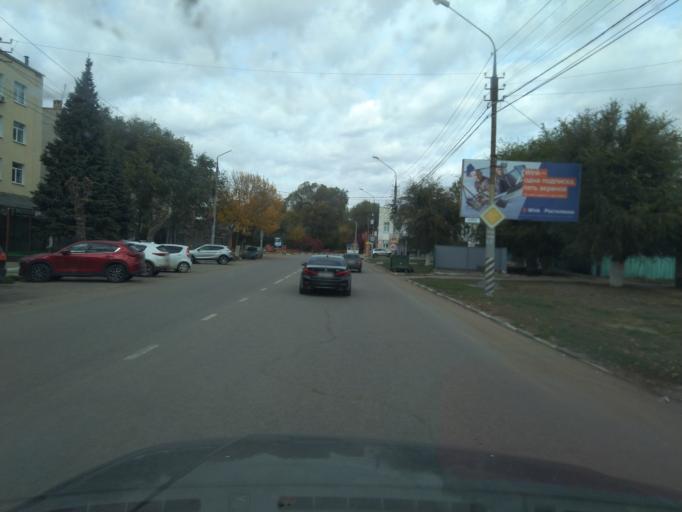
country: RU
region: Saratov
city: Engel's
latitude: 51.4933
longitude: 46.1239
